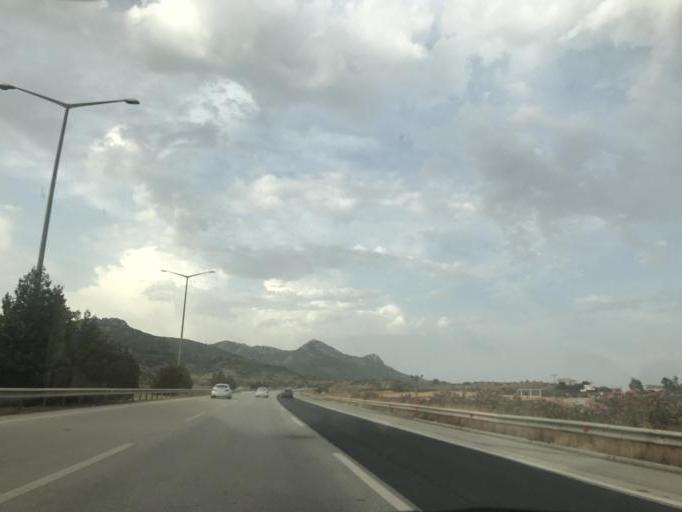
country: TR
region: Adana
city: Ceyhan
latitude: 37.0084
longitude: 35.9577
